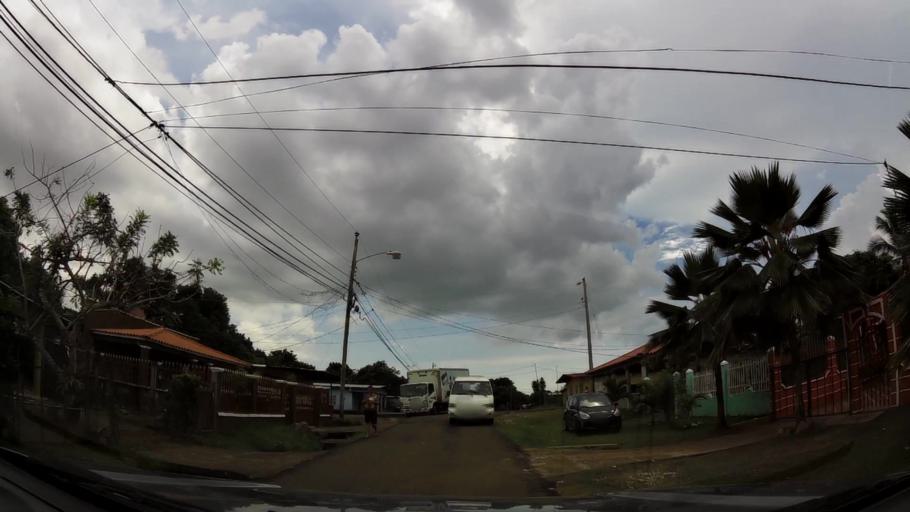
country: PA
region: Panama
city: Cabra Numero Uno
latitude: 9.1089
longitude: -79.3214
